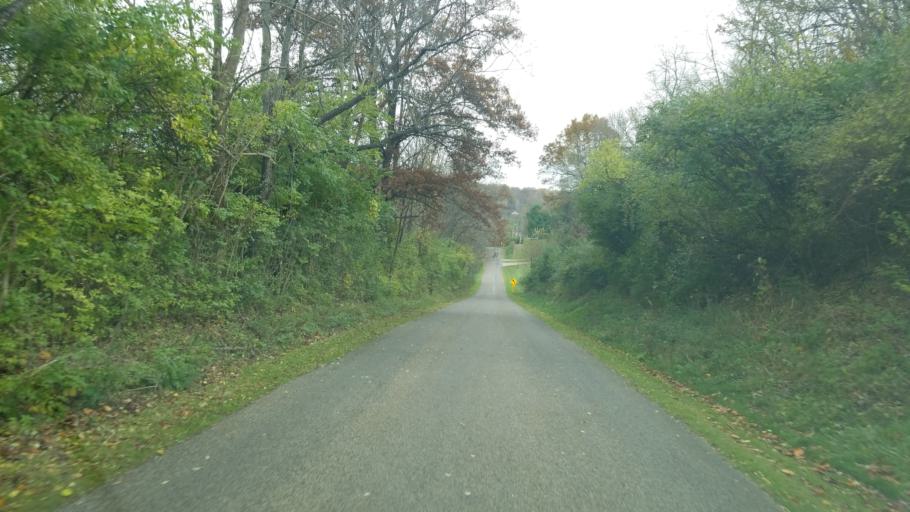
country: US
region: Ohio
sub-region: Richland County
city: Mansfield
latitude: 40.7241
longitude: -82.4955
